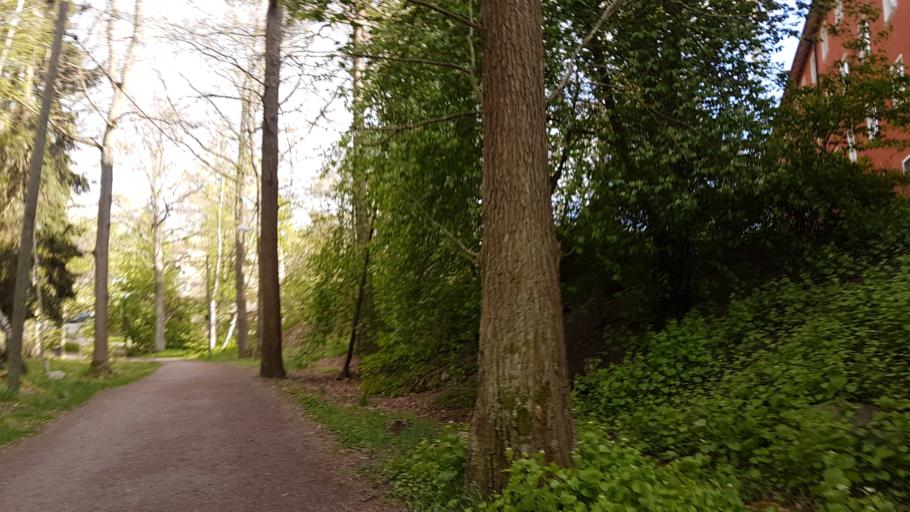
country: SE
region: Stockholm
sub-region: Nacka Kommun
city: Nacka
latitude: 59.2959
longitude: 18.1183
